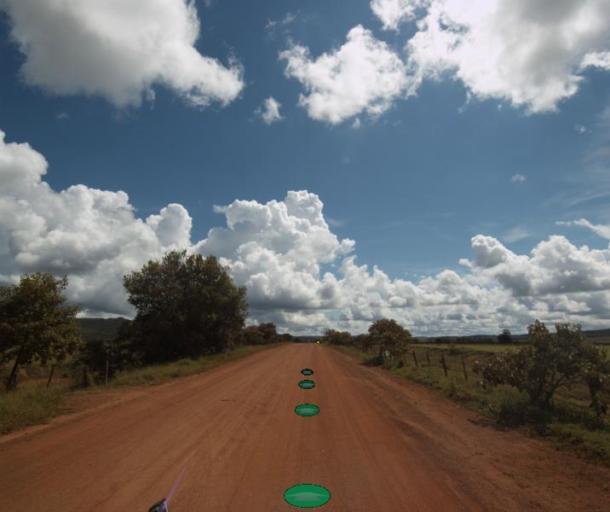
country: BR
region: Goias
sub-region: Pirenopolis
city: Pirenopolis
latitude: -15.7814
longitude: -48.8068
